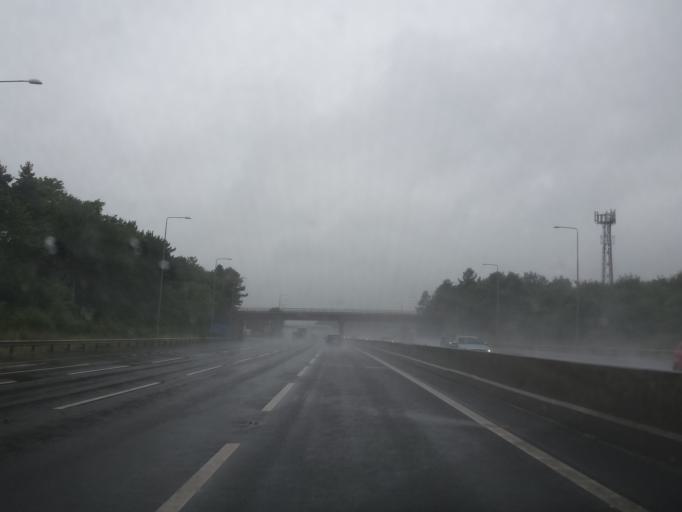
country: GB
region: England
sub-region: Nottinghamshire
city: Kimberley
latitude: 52.9648
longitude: -1.2633
